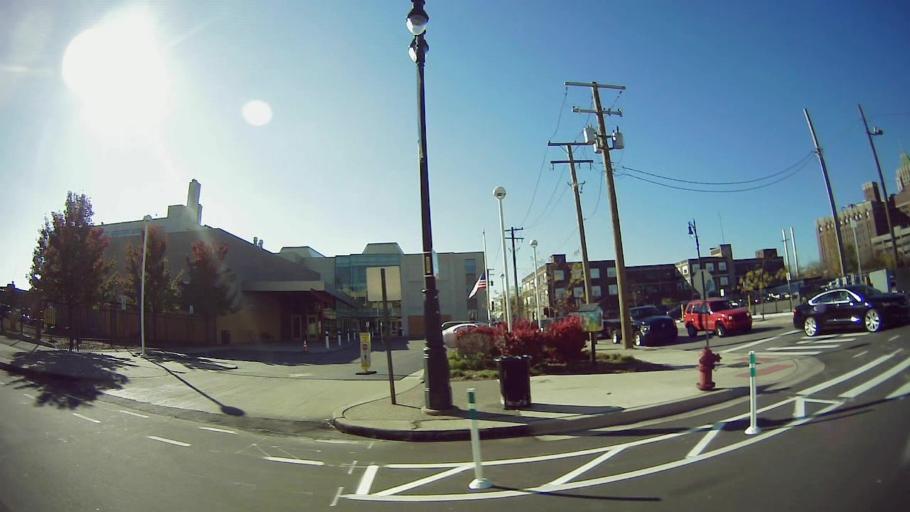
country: US
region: Michigan
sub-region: Wayne County
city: Hamtramck
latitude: 42.3659
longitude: -83.0723
